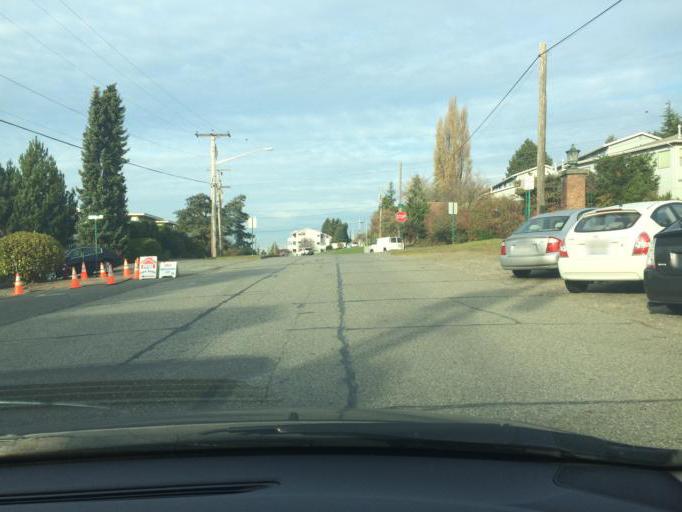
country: US
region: Washington
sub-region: Whatcom County
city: Bellingham
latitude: 48.7221
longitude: -122.5034
